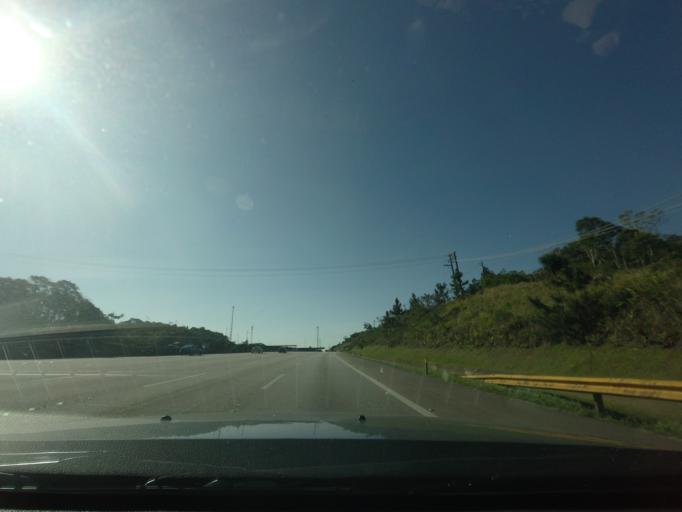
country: BR
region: Sao Paulo
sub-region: Sao Bernardo Do Campo
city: Sao Bernardo do Campo
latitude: -23.8241
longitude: -46.5814
